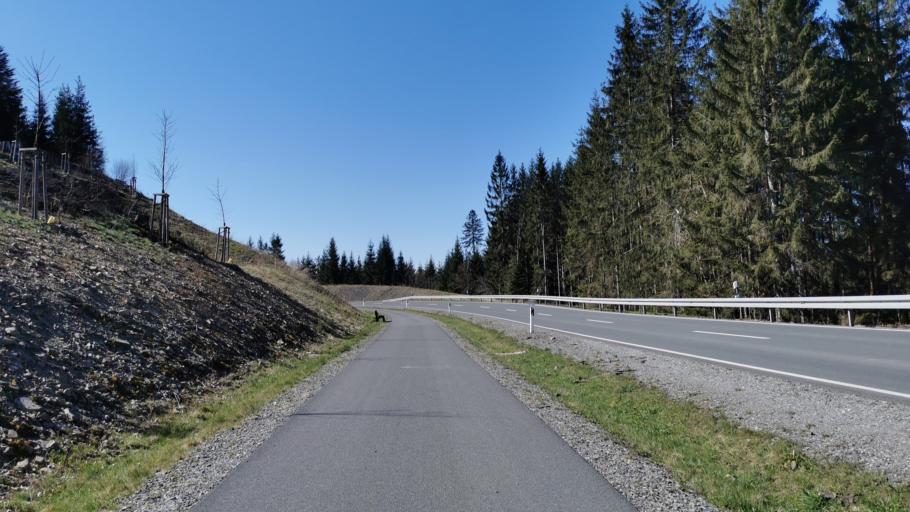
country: DE
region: Bavaria
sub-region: Upper Franconia
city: Teuschnitz
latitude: 50.4201
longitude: 11.3337
